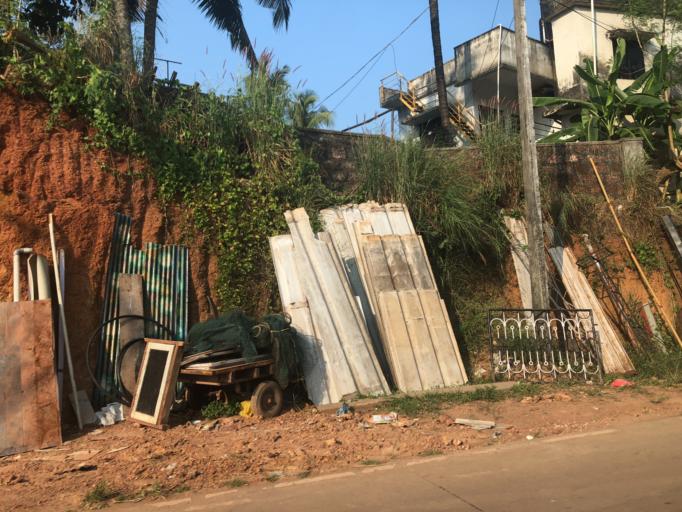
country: IN
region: Karnataka
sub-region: Dakshina Kannada
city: Ullal
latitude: 12.8164
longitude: 74.8485
